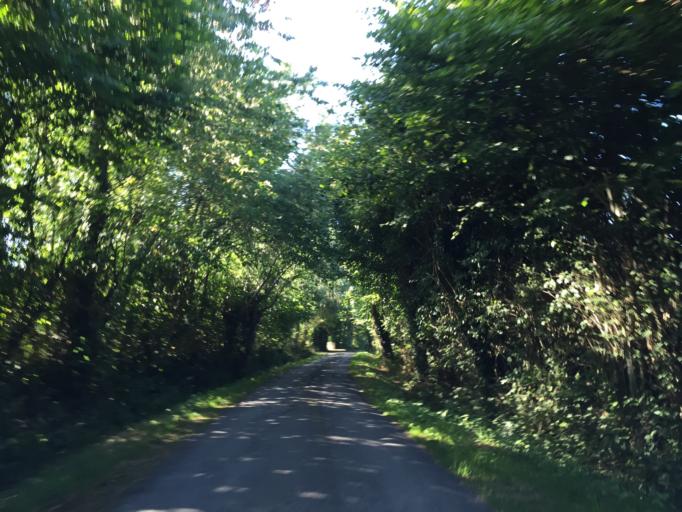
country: FR
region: Lower Normandy
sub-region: Departement du Calvados
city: Equemauville
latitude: 49.4049
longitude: 0.1943
